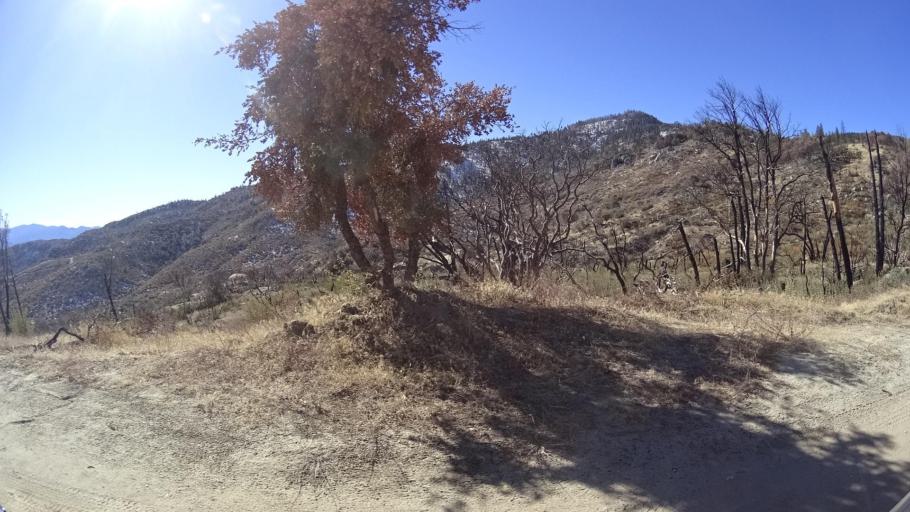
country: US
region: California
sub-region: Kern County
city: Alta Sierra
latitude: 35.7155
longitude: -118.5244
